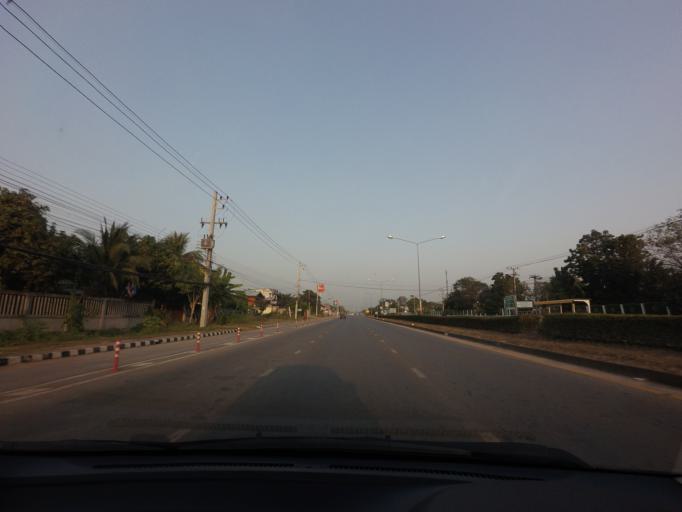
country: TH
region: Sukhothai
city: Sukhothai
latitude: 17.0185
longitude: 99.8573
